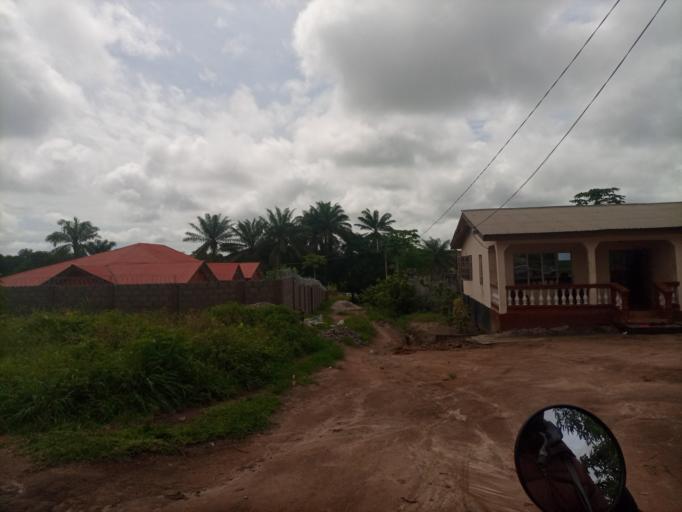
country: SL
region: Northern Province
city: Masoyila
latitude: 8.5929
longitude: -13.1754
